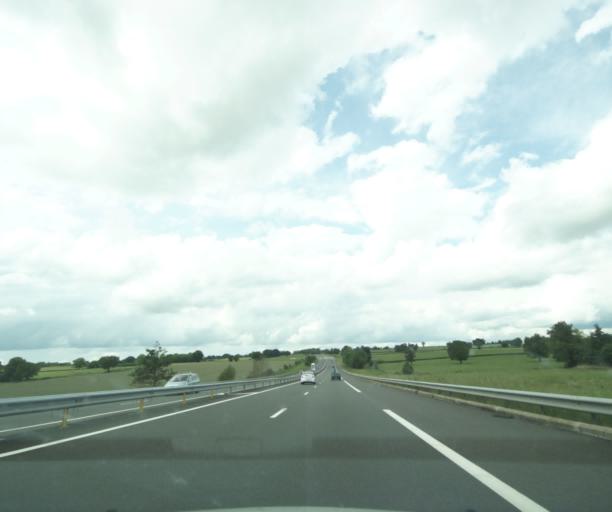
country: FR
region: Auvergne
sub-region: Departement de l'Allier
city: Bellenaves
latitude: 46.2818
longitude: 3.0490
